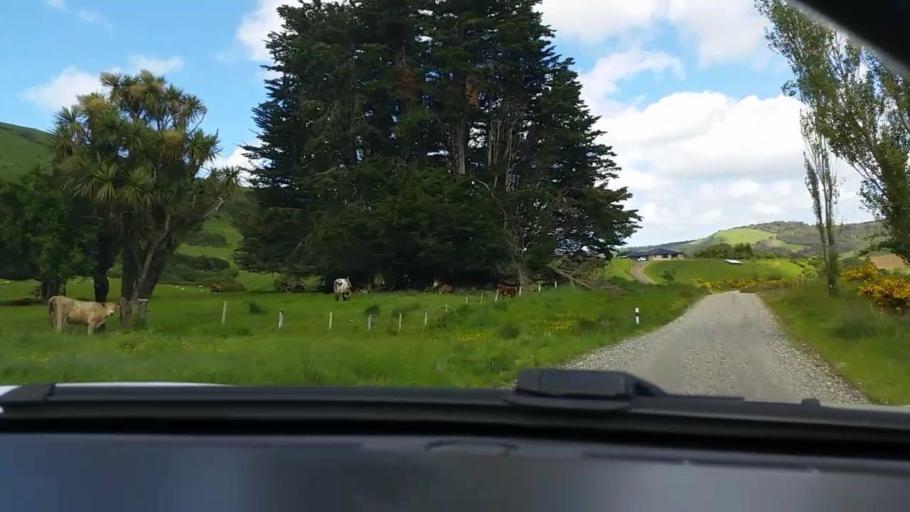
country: NZ
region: Otago
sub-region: Clutha District
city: Papatowai
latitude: -46.5901
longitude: 169.1490
